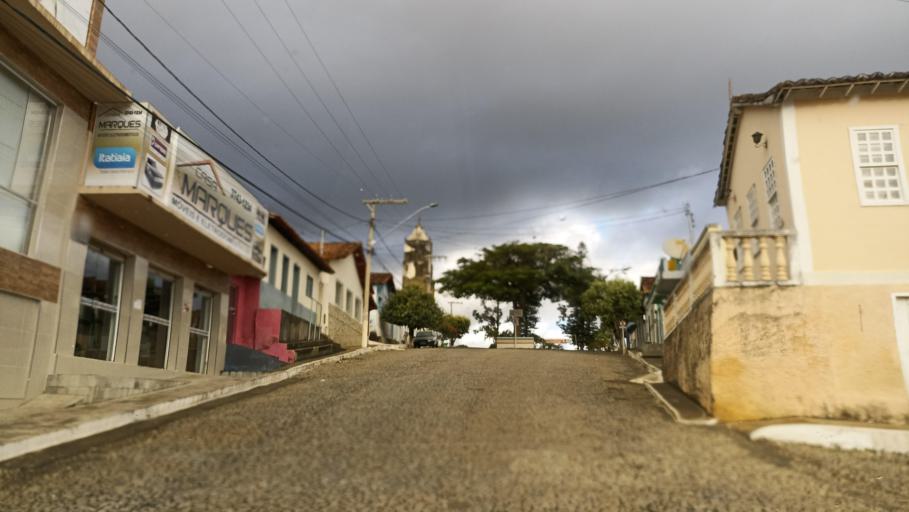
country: BR
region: Minas Gerais
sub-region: Joaima
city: Joaima
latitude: -16.6393
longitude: -40.7624
